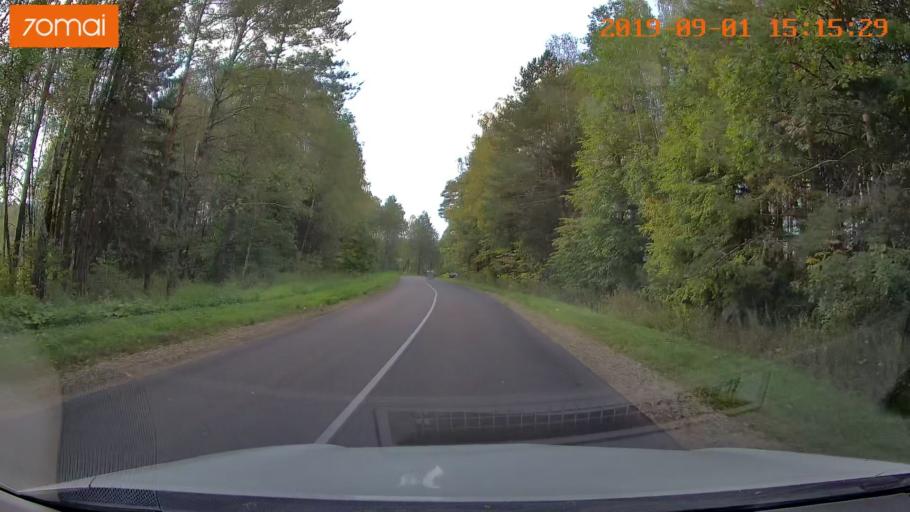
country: RU
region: Kaluga
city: Maloyaroslavets
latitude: 54.8789
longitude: 36.5376
